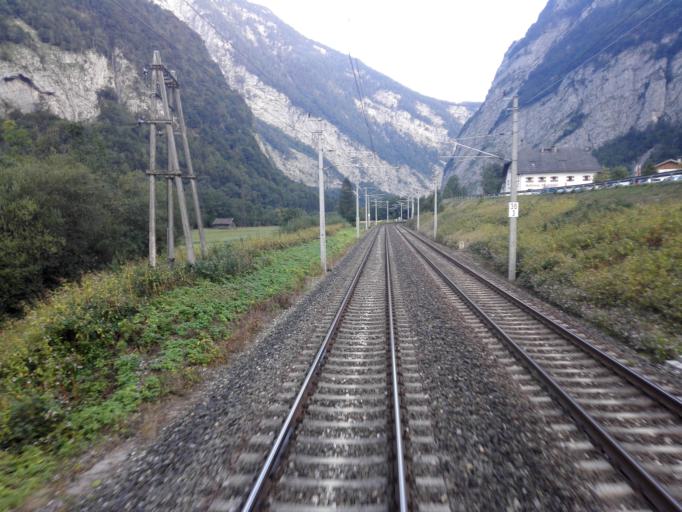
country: AT
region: Salzburg
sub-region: Politischer Bezirk Hallein
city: Golling an der Salzach
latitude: 47.5442
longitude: 13.1705
